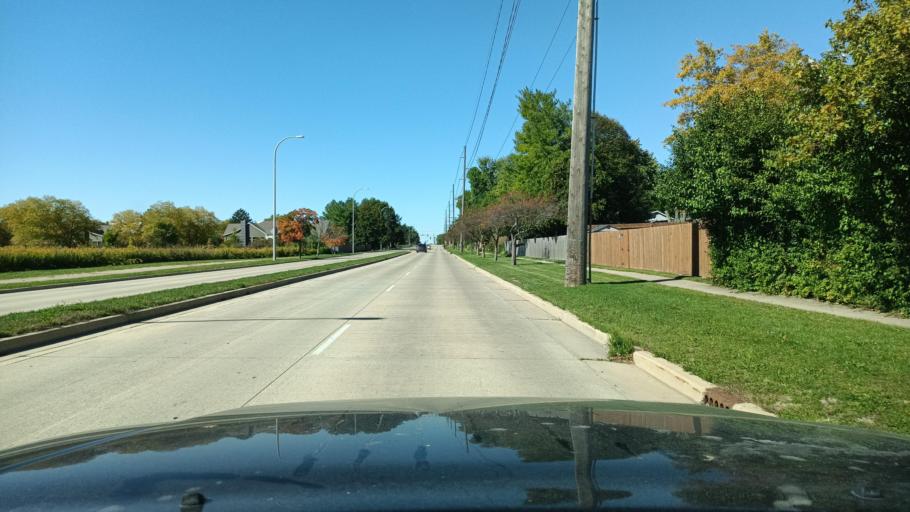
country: US
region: Illinois
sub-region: Champaign County
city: Urbana
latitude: 40.0838
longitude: -88.2032
